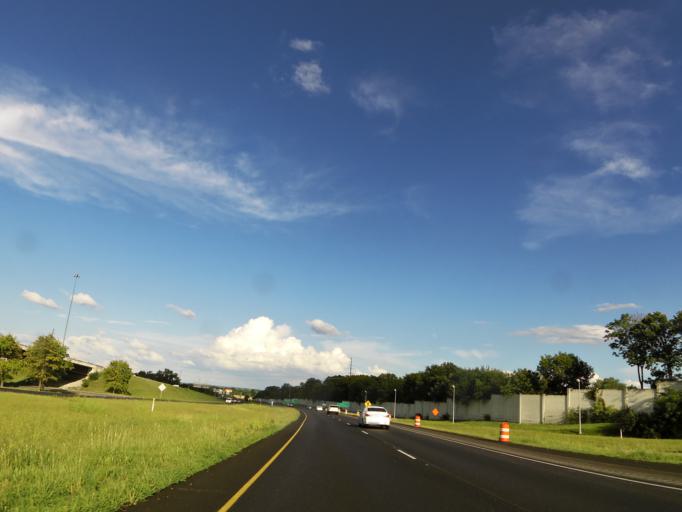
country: US
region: Tennessee
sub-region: Davidson County
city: Nashville
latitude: 36.2384
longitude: -86.7404
